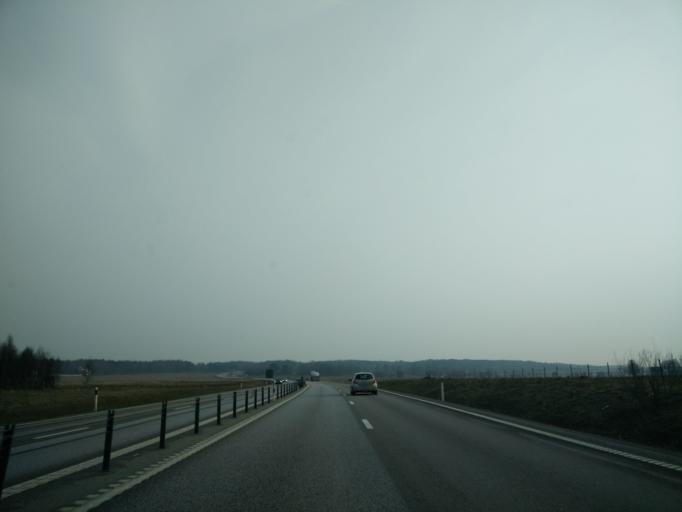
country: SE
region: Vaermland
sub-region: Karlstads Kommun
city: Karlstad
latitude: 59.4223
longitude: 13.4093
